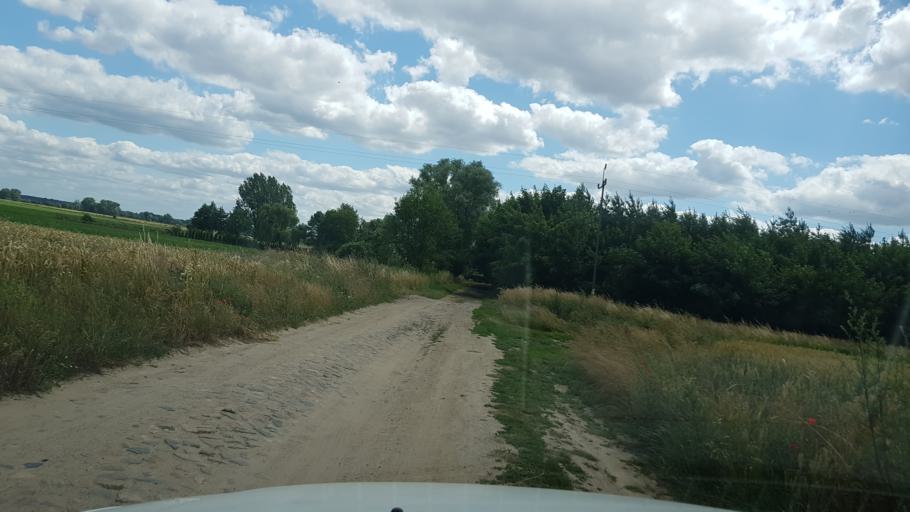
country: PL
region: West Pomeranian Voivodeship
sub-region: Powiat pyrzycki
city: Lipiany
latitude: 52.9656
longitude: 14.9910
